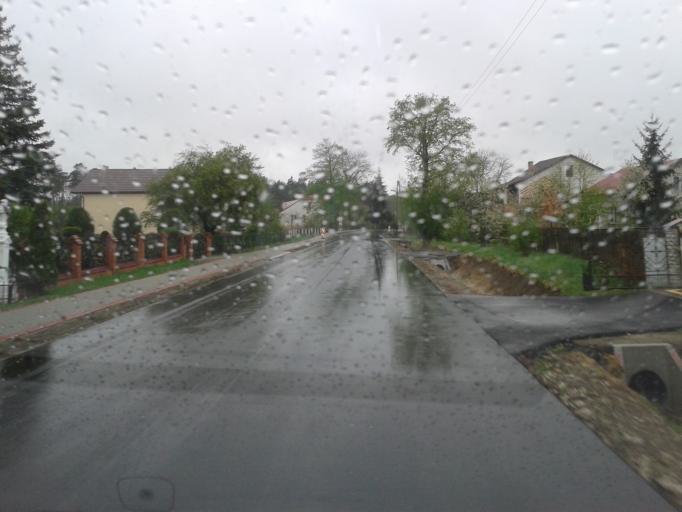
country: PL
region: Lublin Voivodeship
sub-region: Powiat tomaszowski
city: Lubycza Krolewska
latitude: 50.3613
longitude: 23.5464
